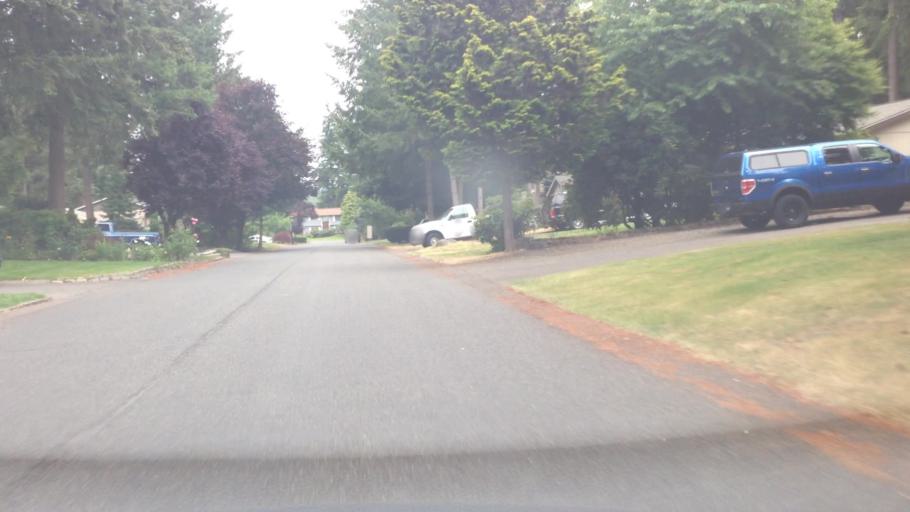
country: US
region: Washington
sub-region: Pierce County
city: South Hill
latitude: 47.1096
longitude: -122.3025
